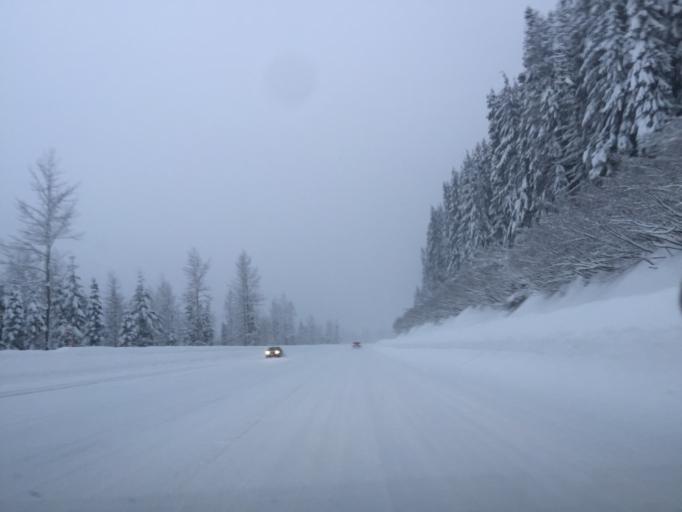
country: US
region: Washington
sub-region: Chelan County
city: Leavenworth
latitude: 47.7709
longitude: -121.0762
